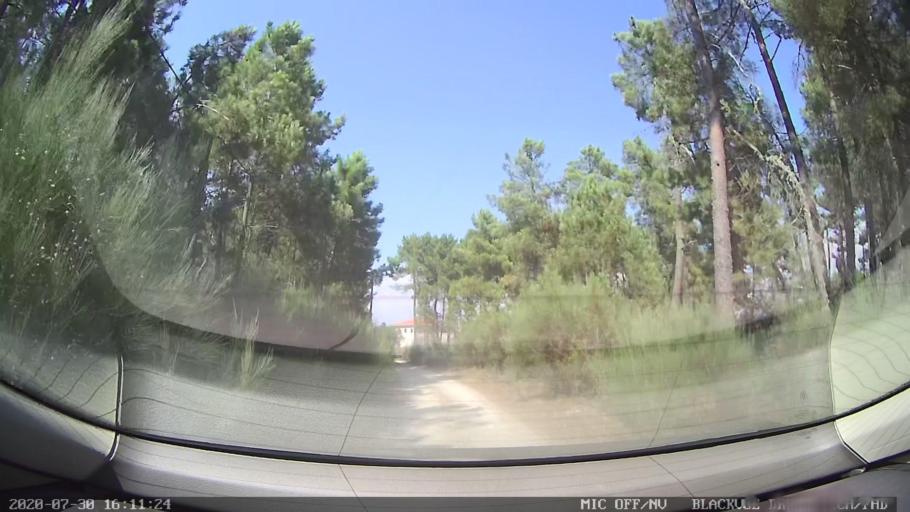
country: PT
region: Vila Real
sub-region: Murca
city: Murca
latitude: 41.3442
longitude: -7.4741
